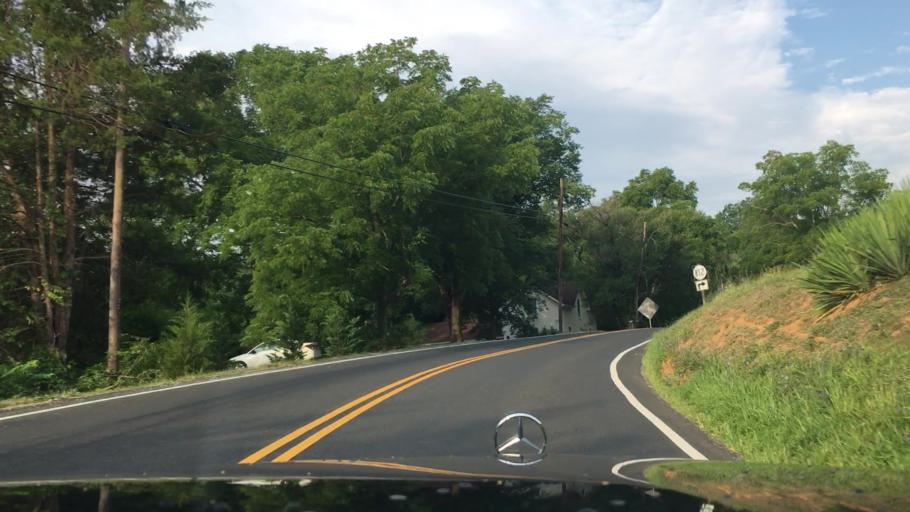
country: US
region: Virginia
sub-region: Campbell County
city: Timberlake
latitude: 37.2343
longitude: -79.2886
